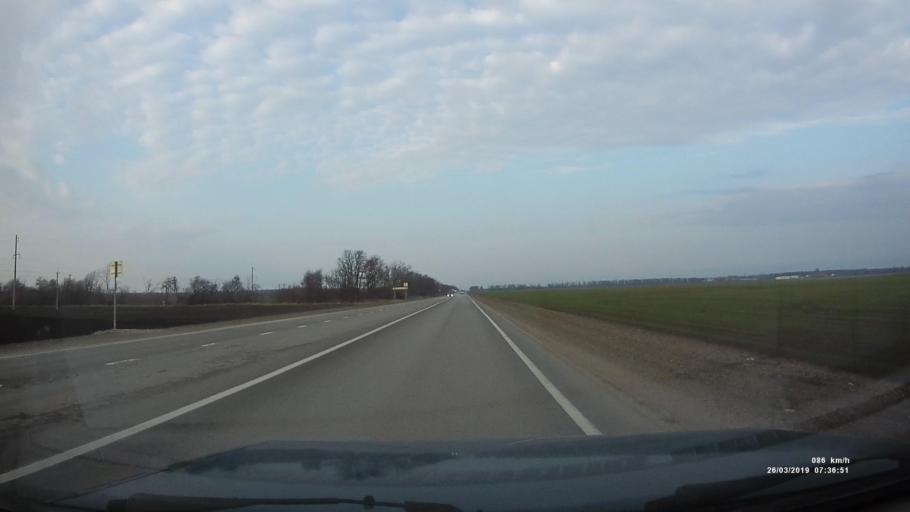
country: RU
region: Rostov
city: Novobessergenovka
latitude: 47.2039
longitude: 38.7130
